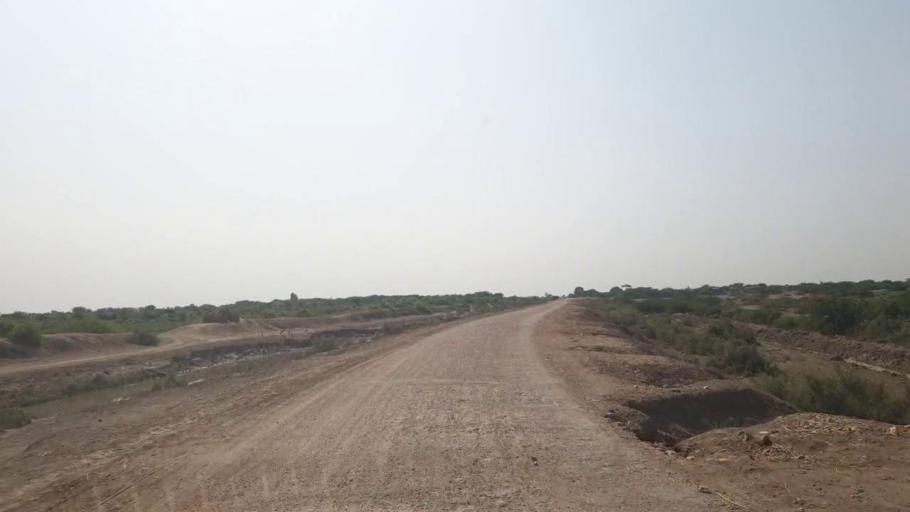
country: PK
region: Sindh
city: Kadhan
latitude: 24.4641
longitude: 68.9057
